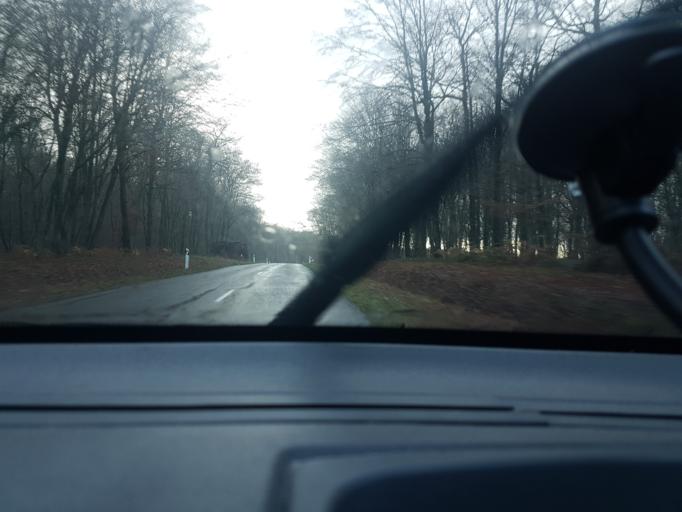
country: FR
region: Franche-Comte
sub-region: Territoire de Belfort
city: Danjoutin
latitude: 47.6100
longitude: 6.8510
